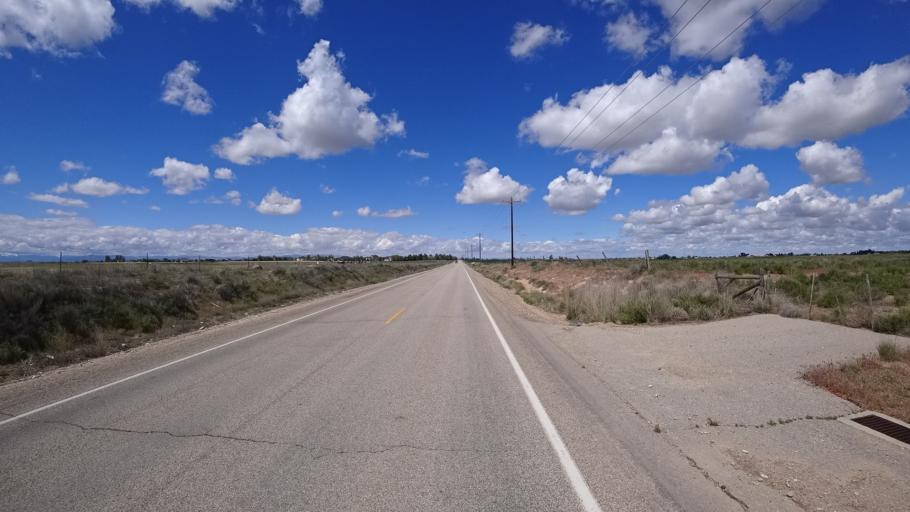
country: US
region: Idaho
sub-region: Ada County
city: Kuna
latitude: 43.4592
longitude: -116.3196
